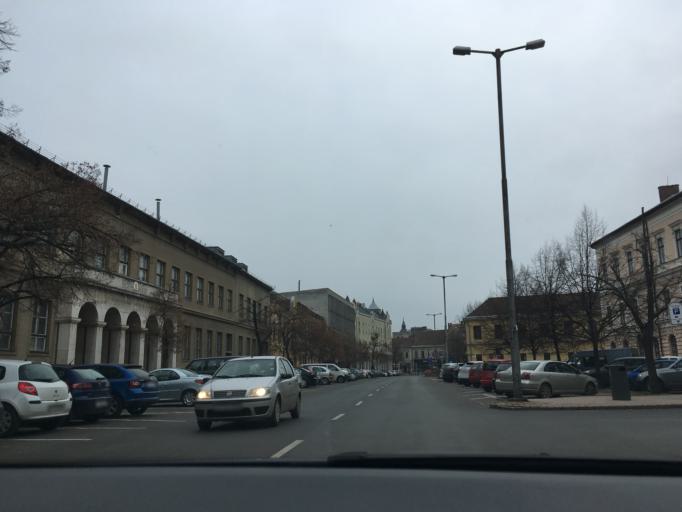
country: HU
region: Hajdu-Bihar
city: Debrecen
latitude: 47.5307
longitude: 21.6261
